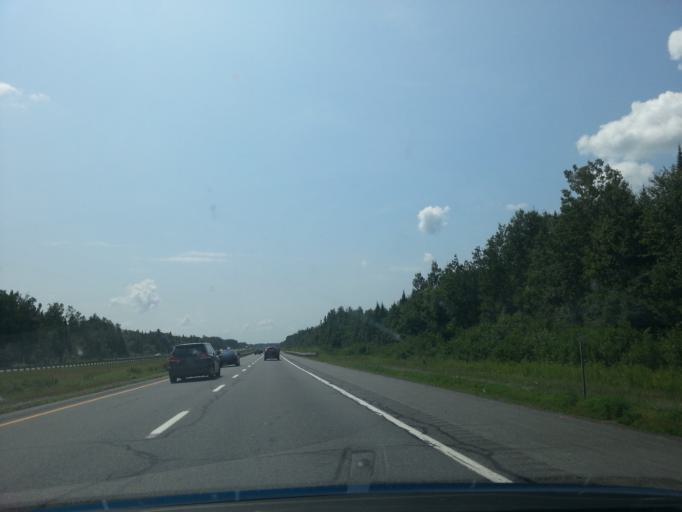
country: CA
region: Quebec
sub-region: Mauricie
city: Princeville
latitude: 46.3351
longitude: -71.9168
